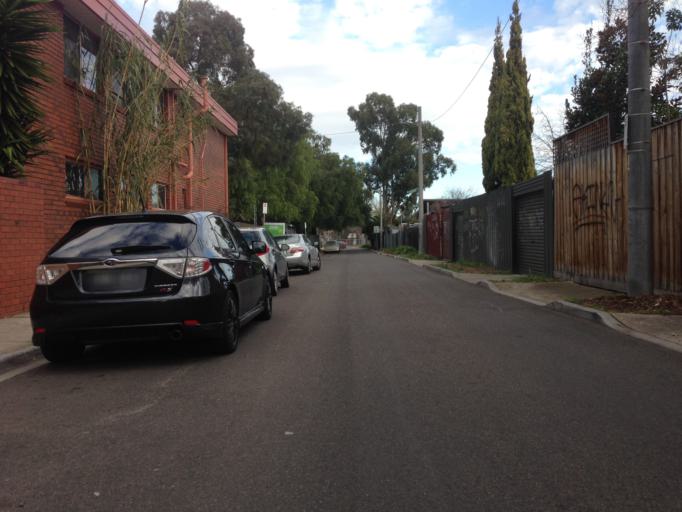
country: AU
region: Victoria
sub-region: Darebin
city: Fairfield
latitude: -37.7774
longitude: 145.0201
